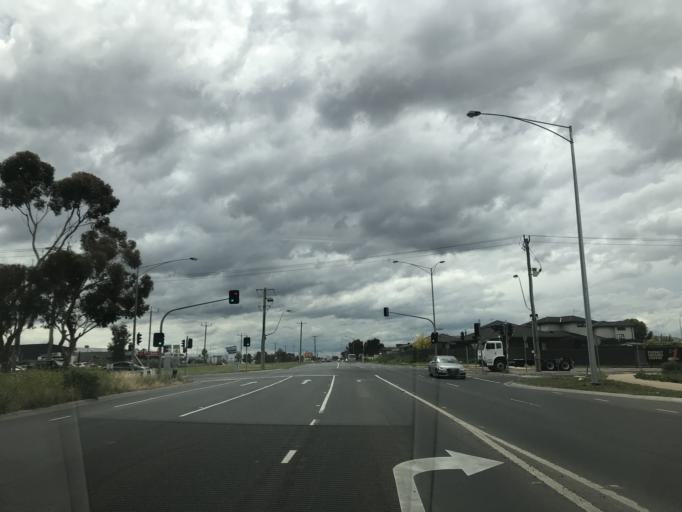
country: AU
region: Victoria
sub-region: Brimbank
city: Derrimut
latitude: -37.7819
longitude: 144.7547
